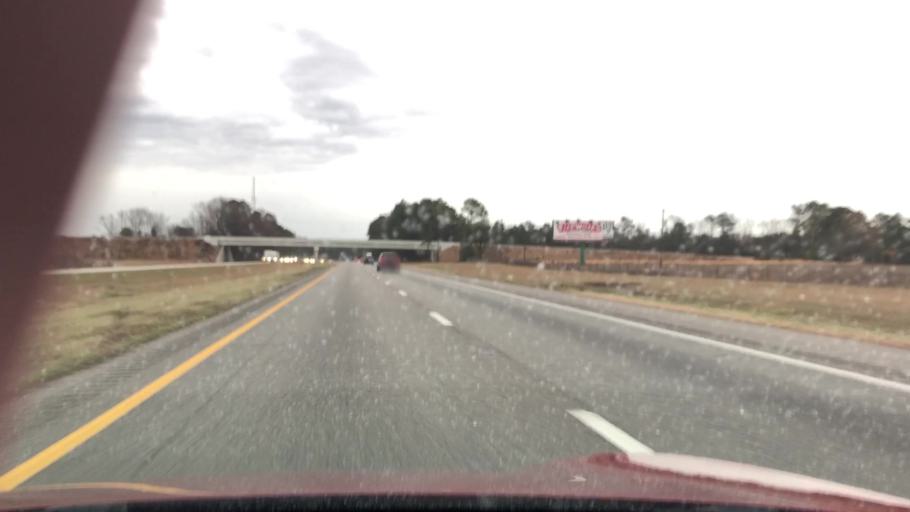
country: US
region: South Carolina
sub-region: Dillon County
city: Latta
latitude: 34.3651
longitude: -79.4977
